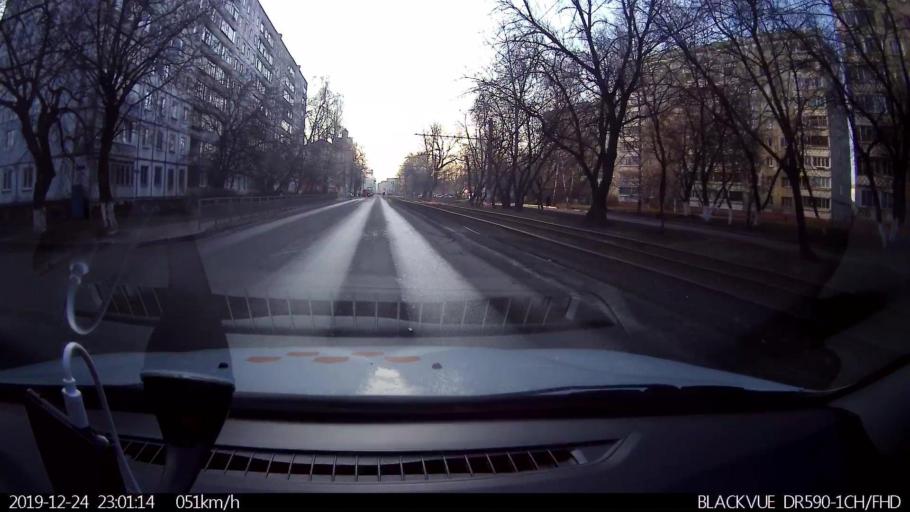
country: RU
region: Nizjnij Novgorod
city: Nizhniy Novgorod
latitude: 56.2693
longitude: 43.9284
